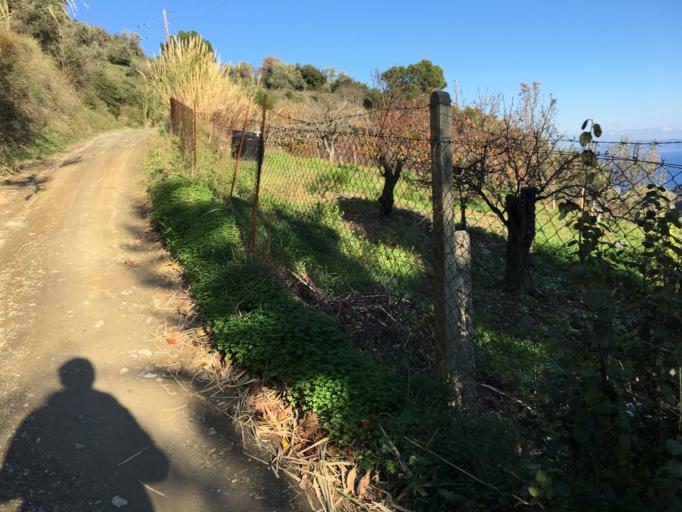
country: GR
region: Thessaly
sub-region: Nomos Magnisias
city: Skopelos
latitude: 39.1800
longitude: 23.6258
